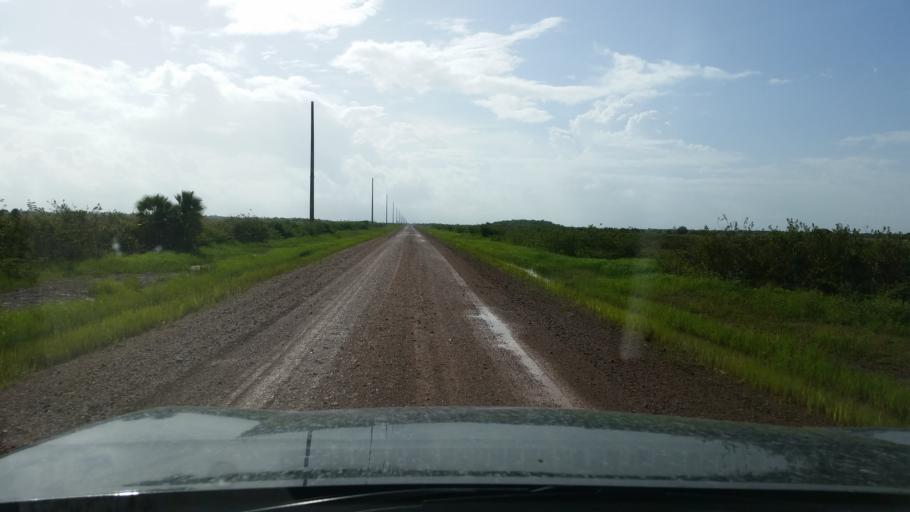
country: NI
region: Atlantico Norte (RAAN)
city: Puerto Cabezas
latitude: 14.1099
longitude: -83.6024
